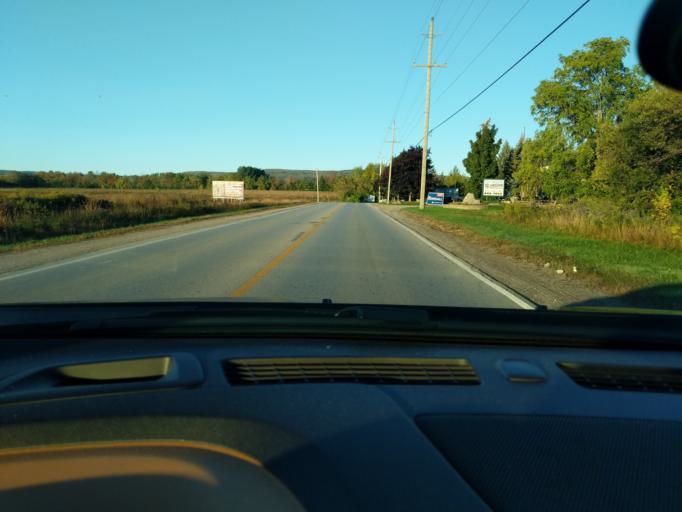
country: CA
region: Ontario
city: Collingwood
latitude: 44.4992
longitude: -80.2533
